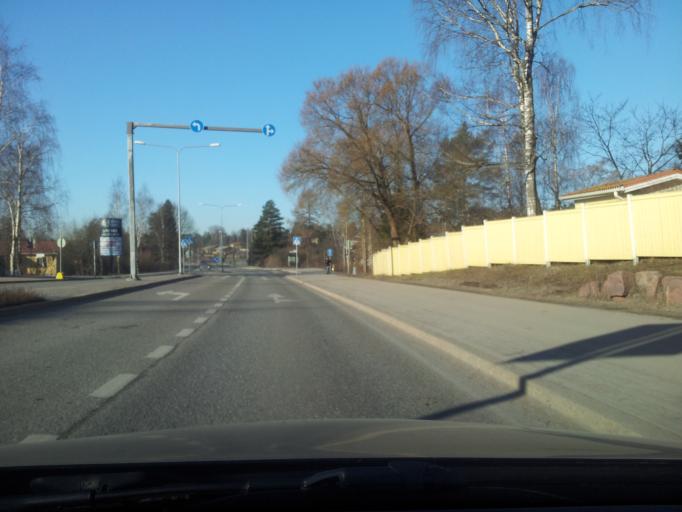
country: FI
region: Uusimaa
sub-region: Helsinki
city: Kauniainen
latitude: 60.1620
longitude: 24.6993
